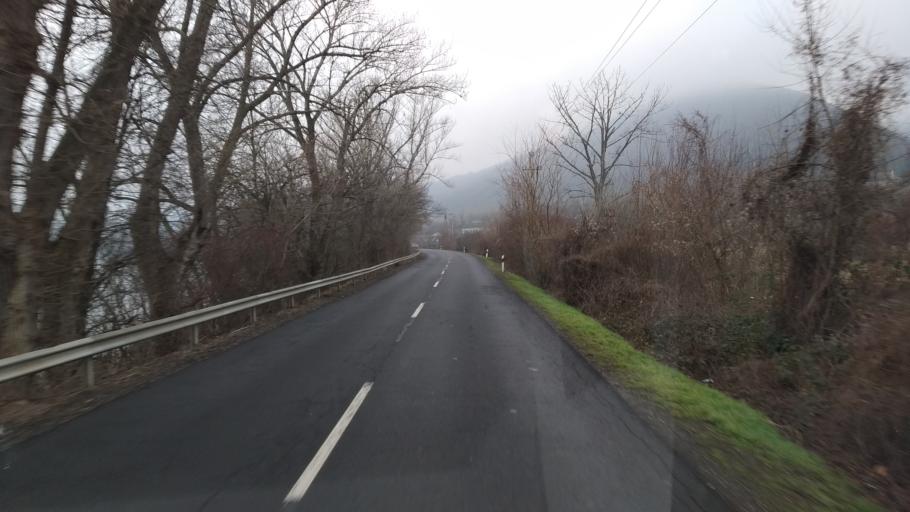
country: HU
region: Pest
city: Nagymaros
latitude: 47.7621
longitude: 18.9261
